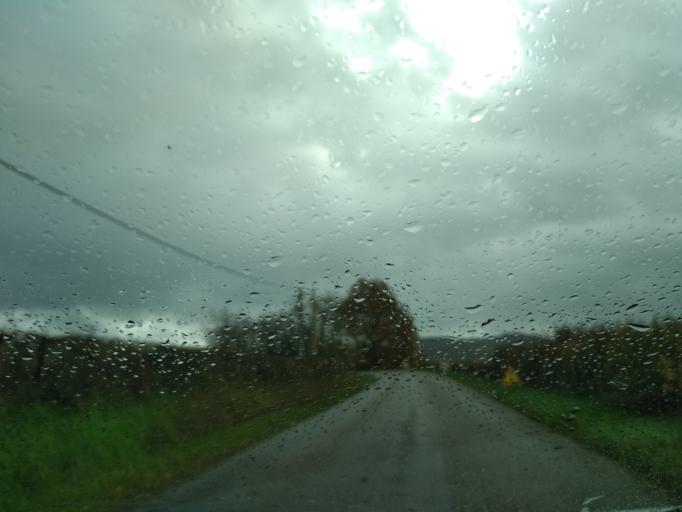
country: FR
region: Bourgogne
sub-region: Departement de Saone-et-Loire
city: Saint-Leger-sur-Dheune
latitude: 46.8216
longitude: 4.6056
